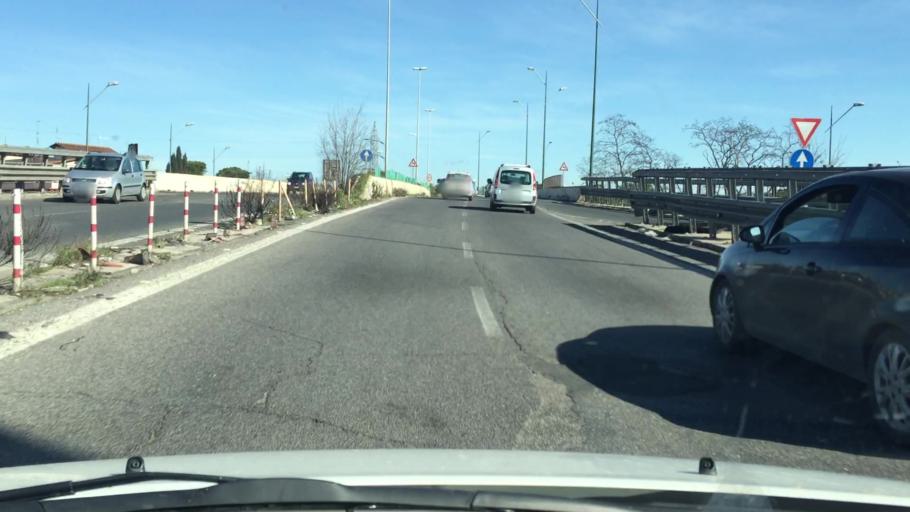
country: IT
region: Latium
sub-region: Citta metropolitana di Roma Capitale
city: Monte Caminetto
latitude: 41.9869
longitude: 12.4932
